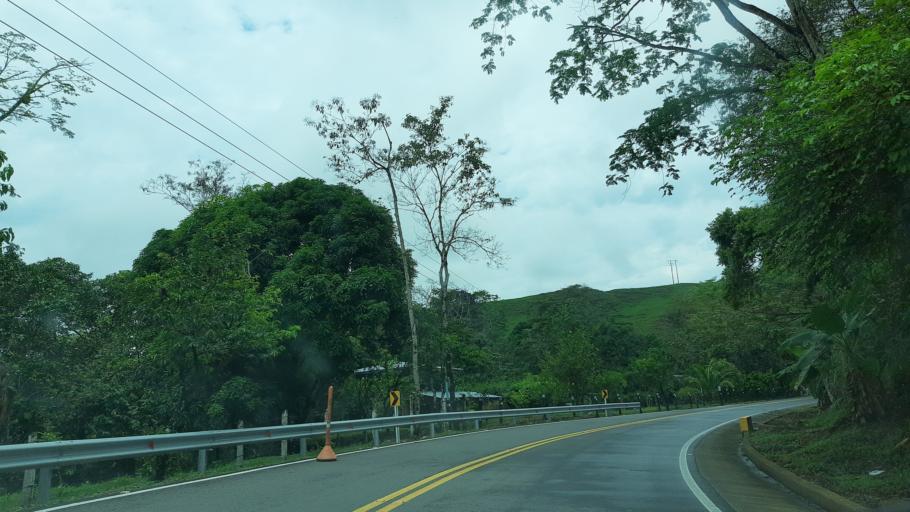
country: CO
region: Casanare
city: Sabanalarga
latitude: 4.7890
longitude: -73.0527
